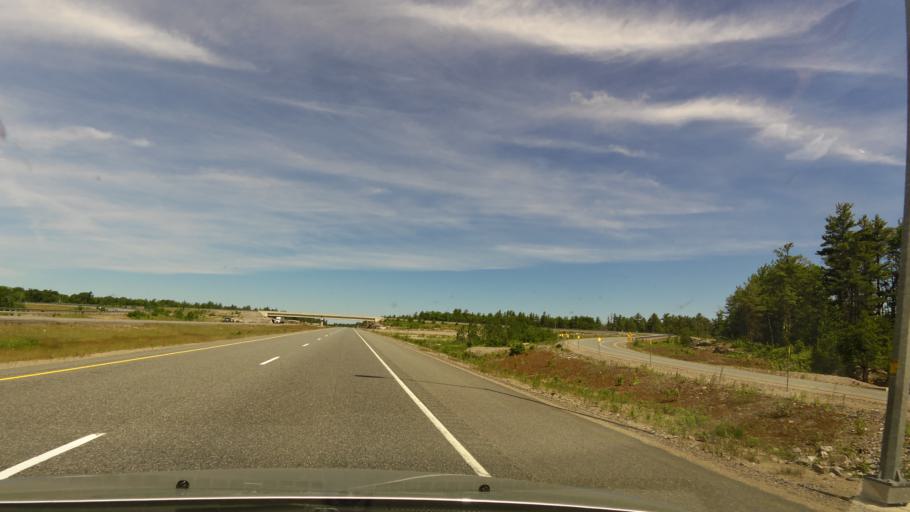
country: CA
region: Ontario
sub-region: Parry Sound District
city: Parry Sound
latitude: 45.4186
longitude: -80.0704
